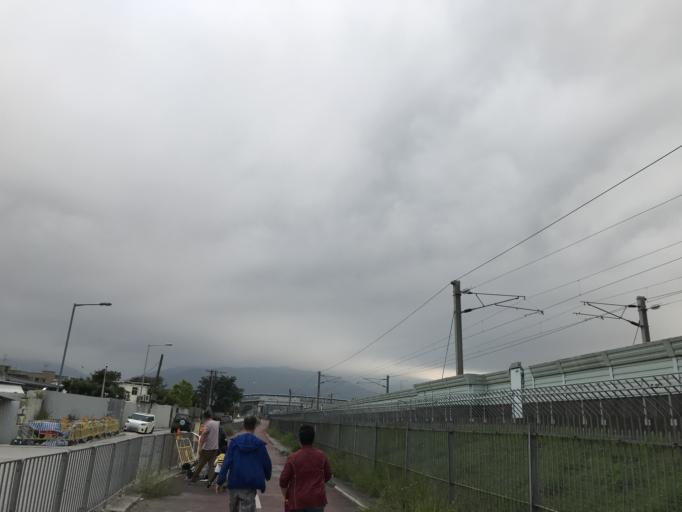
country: HK
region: Tai Po
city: Tai Po
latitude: 22.4781
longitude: 114.1550
